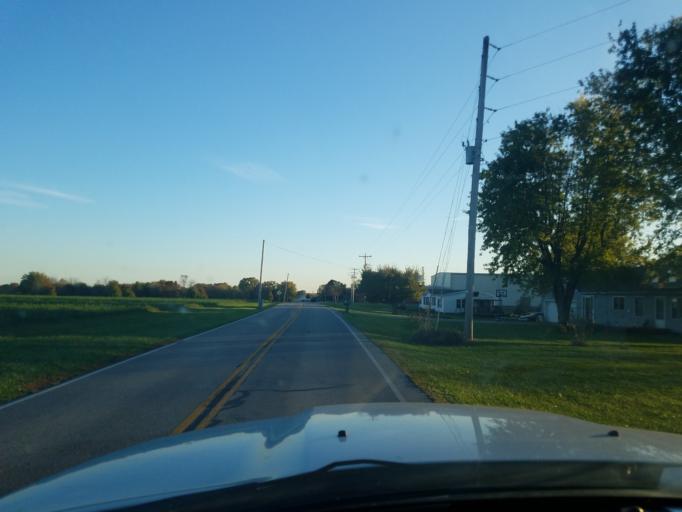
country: US
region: Indiana
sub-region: Floyd County
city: Galena
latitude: 38.3877
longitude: -85.9063
